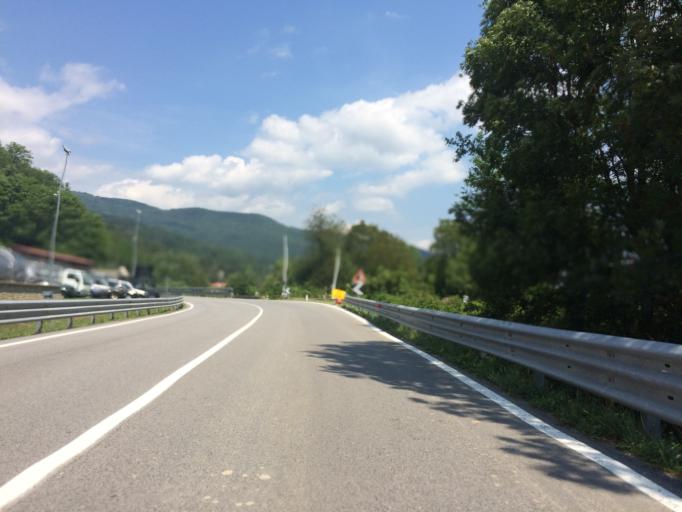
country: IT
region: Piedmont
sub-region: Provincia di Cuneo
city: Priola
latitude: 44.2507
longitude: 8.0216
